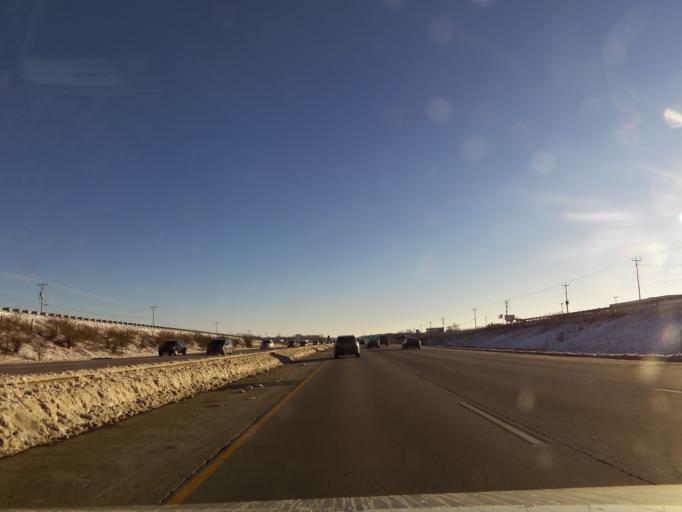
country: US
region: Wisconsin
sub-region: Racine County
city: Franksville
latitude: 42.7578
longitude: -87.9543
